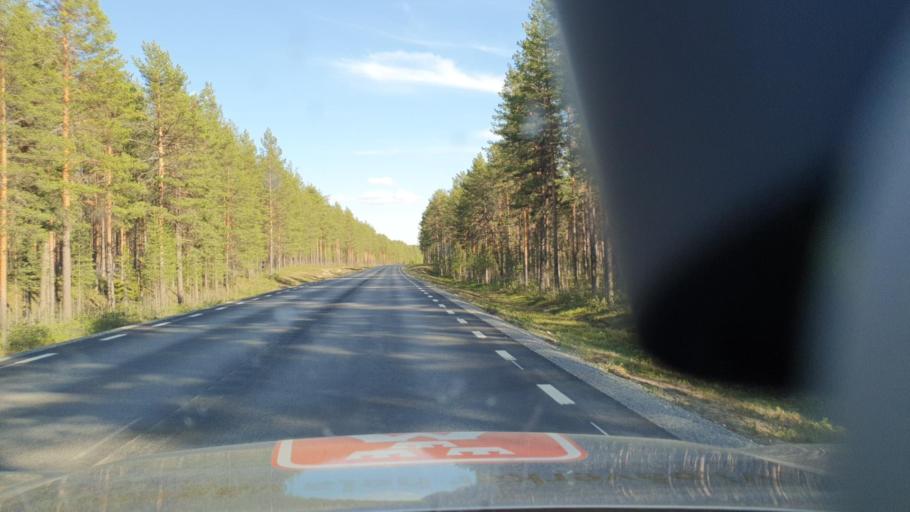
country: SE
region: Norrbotten
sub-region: Alvsbyns Kommun
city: AElvsbyn
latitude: 66.1392
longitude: 20.8878
